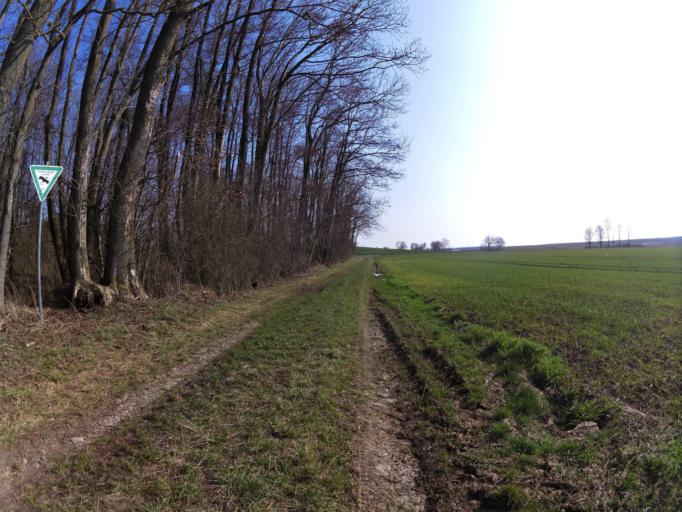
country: DE
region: Bavaria
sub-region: Regierungsbezirk Unterfranken
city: Sulzdorf
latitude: 49.6487
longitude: 9.9133
